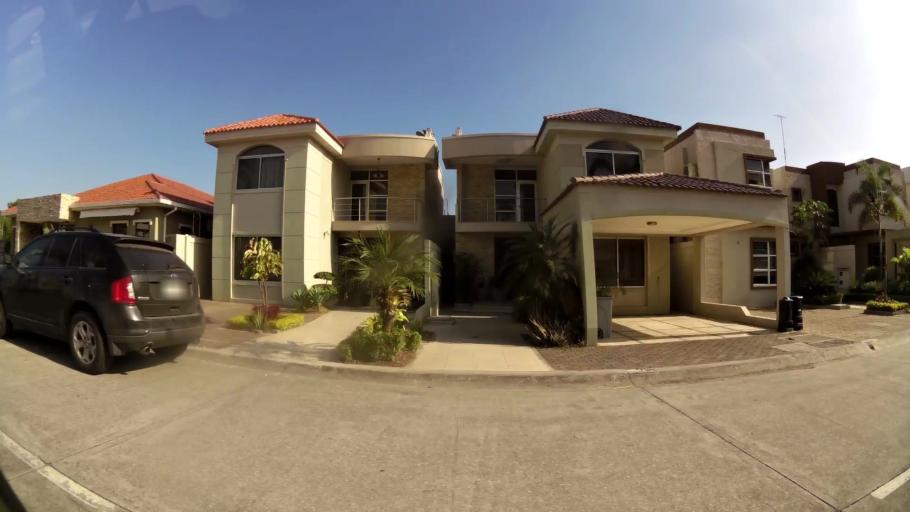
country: EC
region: Guayas
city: Santa Lucia
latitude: -2.1877
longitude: -79.9871
